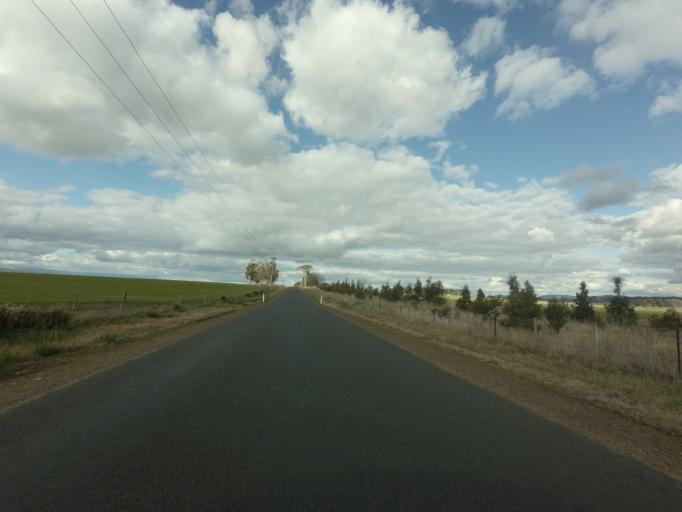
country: AU
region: Tasmania
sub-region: Northern Midlands
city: Longford
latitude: -41.8066
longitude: 147.1714
